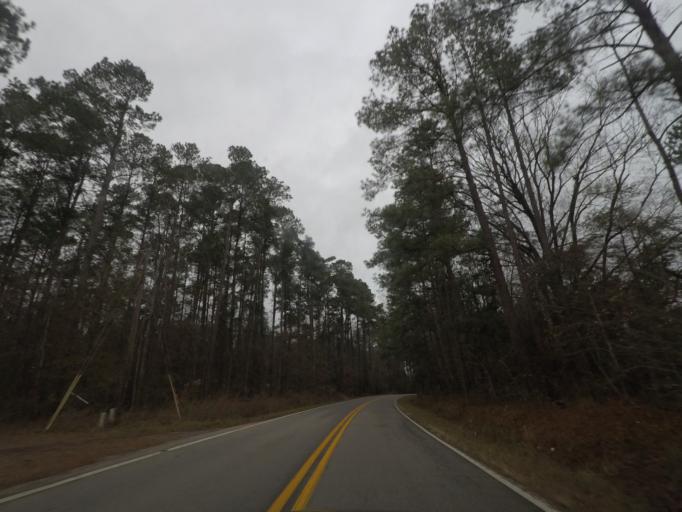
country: US
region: South Carolina
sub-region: Colleton County
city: Walterboro
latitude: 32.9204
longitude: -80.5356
